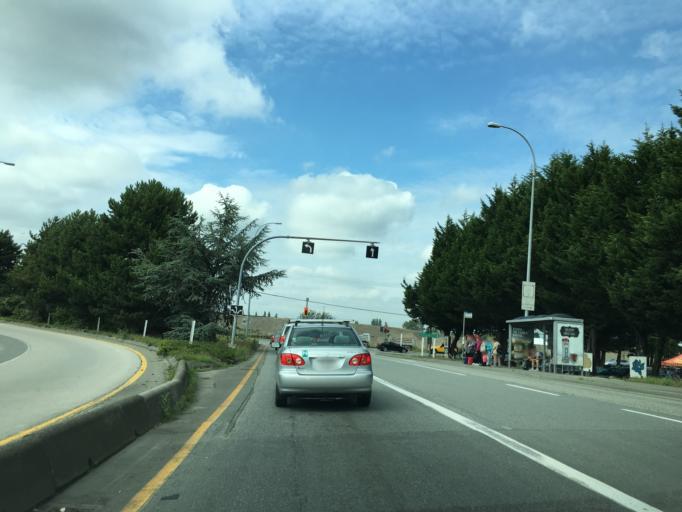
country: CA
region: British Columbia
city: Ladner
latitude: 49.1328
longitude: -123.0845
